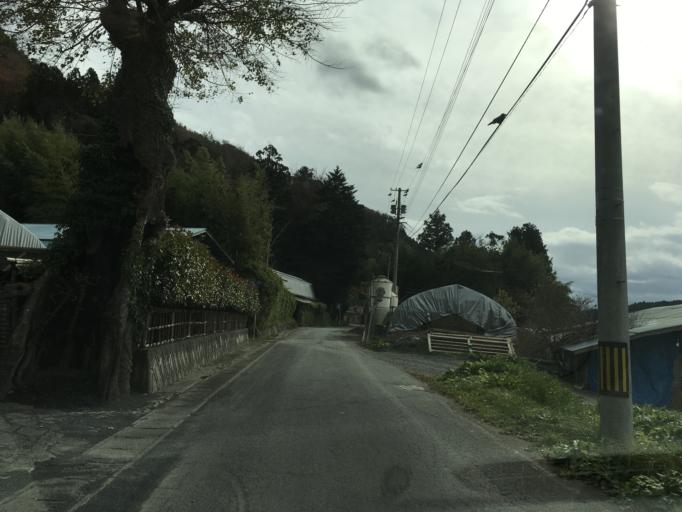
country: JP
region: Iwate
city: Ichinoseki
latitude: 38.7814
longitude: 141.2674
